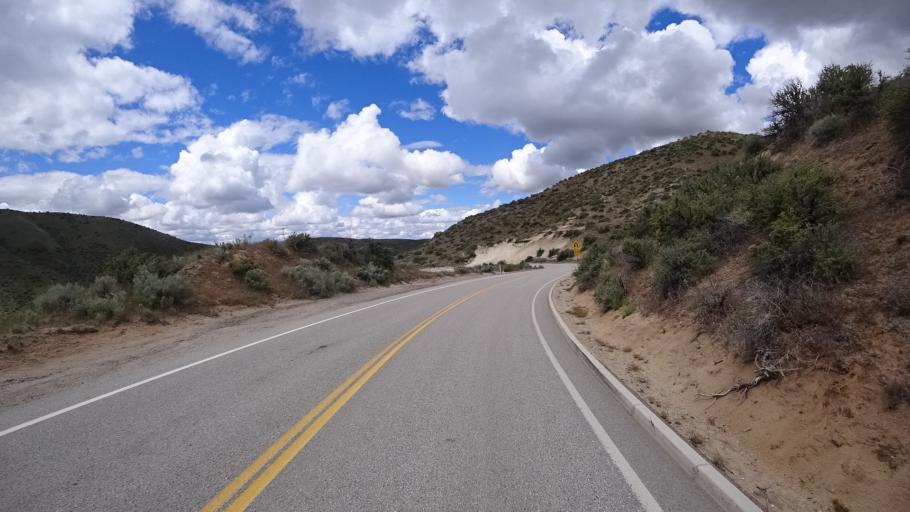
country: US
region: Idaho
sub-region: Ada County
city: Boise
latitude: 43.6894
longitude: -116.1844
